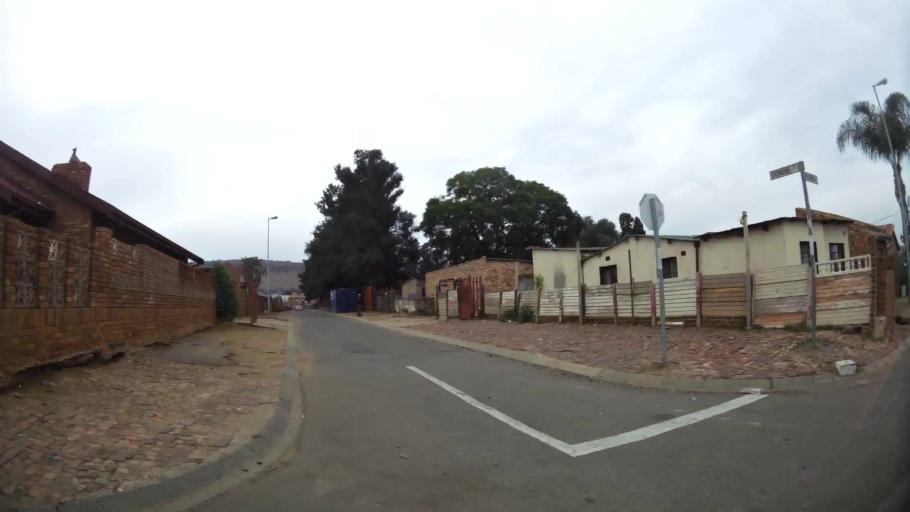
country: ZA
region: Gauteng
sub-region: City of Tshwane Metropolitan Municipality
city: Pretoria
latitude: -25.7071
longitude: 28.3352
